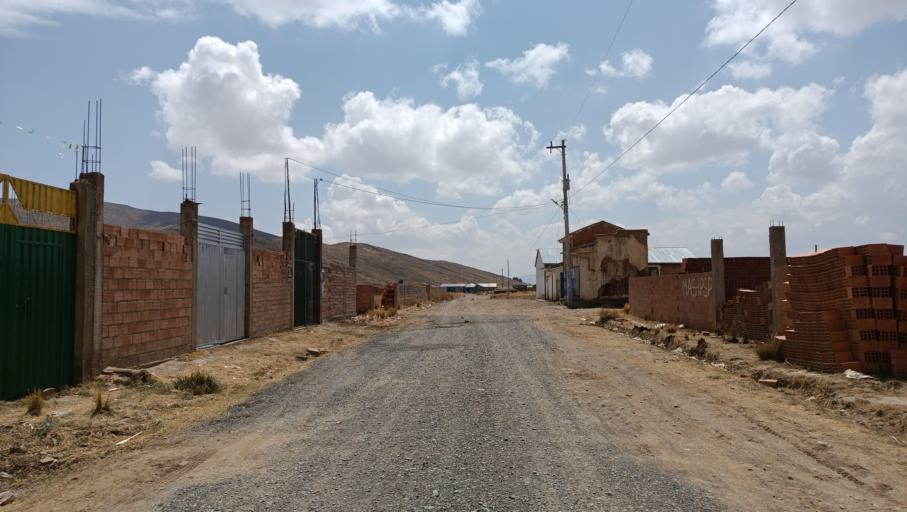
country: BO
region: La Paz
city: Batallas
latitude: -16.4069
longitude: -68.5408
